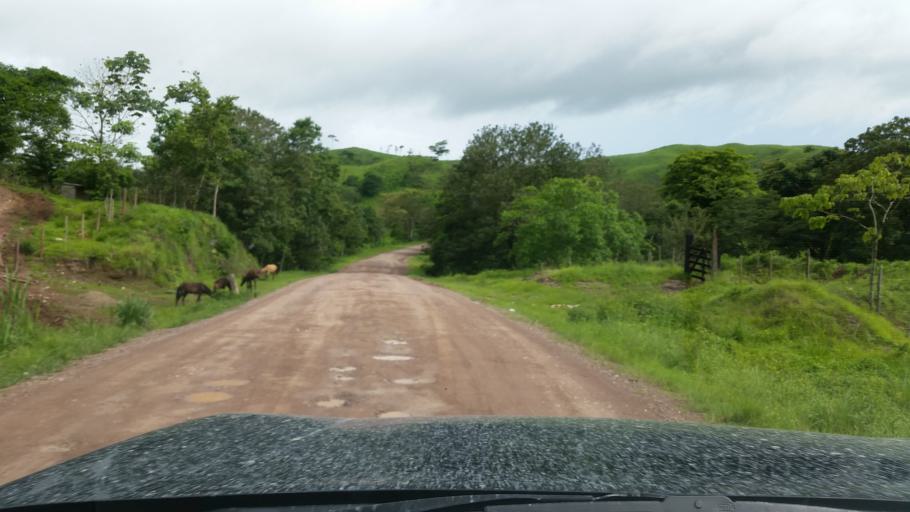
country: NI
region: Atlantico Norte (RAAN)
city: Siuna
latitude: 13.5277
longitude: -84.8230
